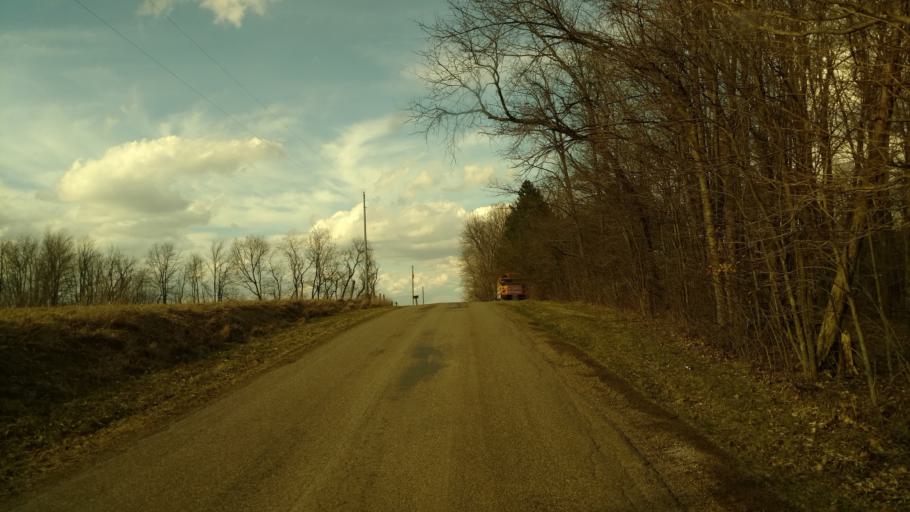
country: US
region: Ohio
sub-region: Sandusky County
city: Bellville
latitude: 40.5533
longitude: -82.4331
